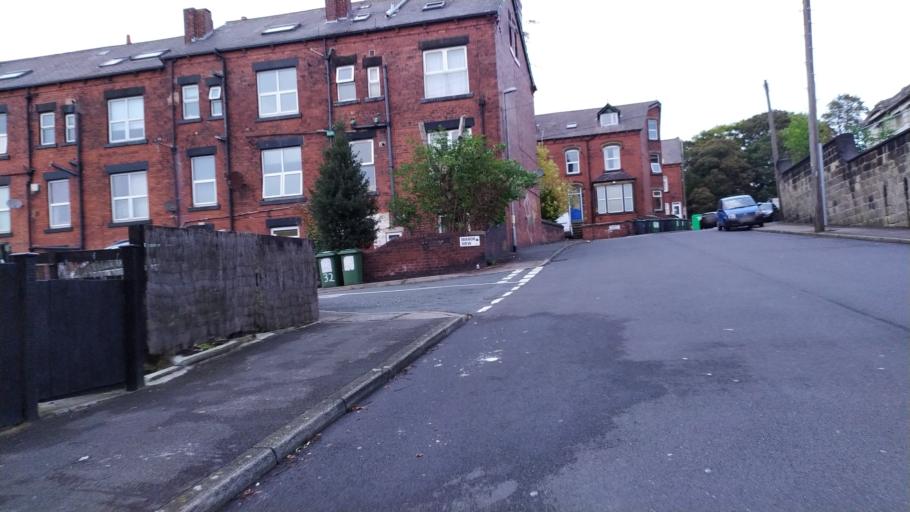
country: GB
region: England
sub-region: City and Borough of Leeds
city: Leeds
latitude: 53.8165
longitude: -1.5718
